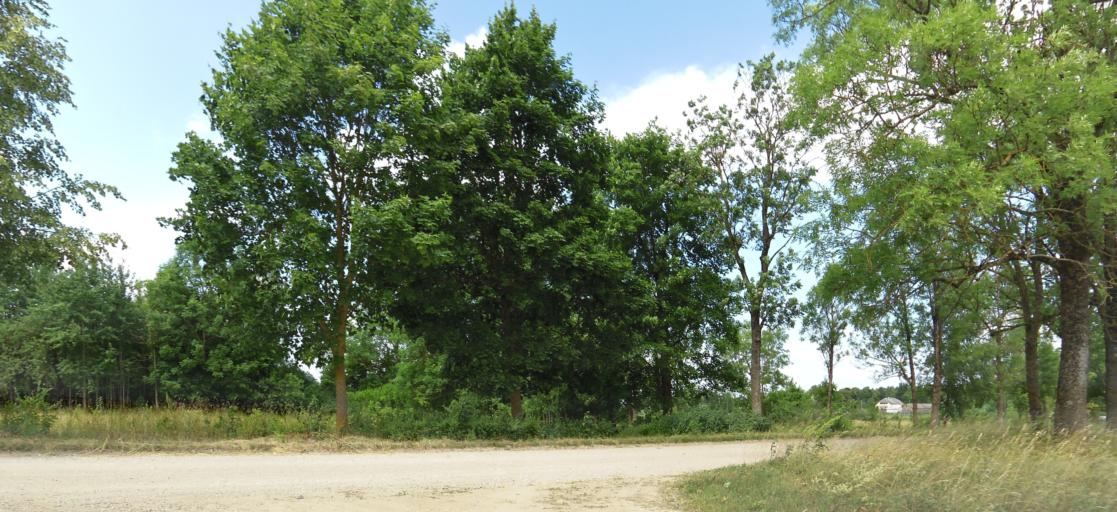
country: LT
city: Obeliai
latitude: 56.1472
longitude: 25.0448
